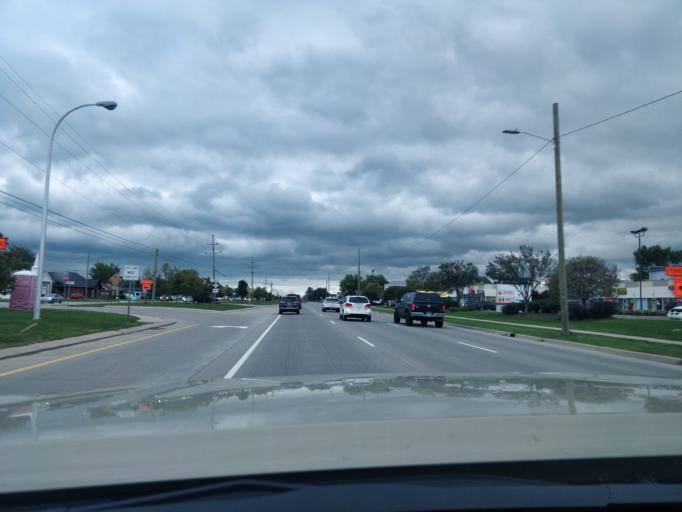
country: US
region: Michigan
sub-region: Wayne County
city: Riverview
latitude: 42.1841
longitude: -83.1897
